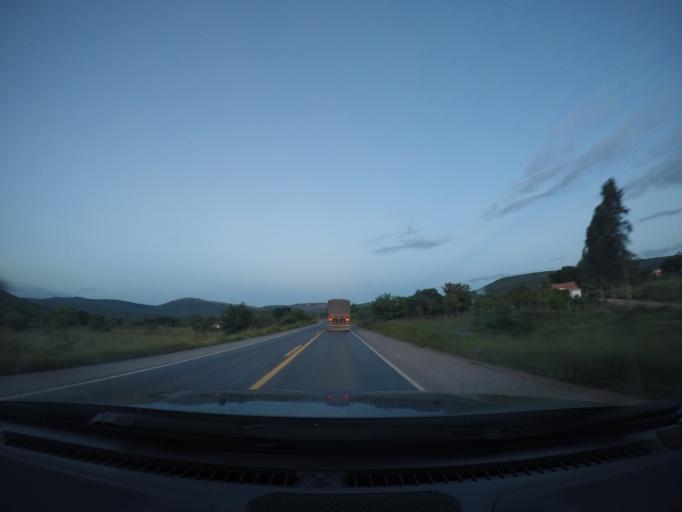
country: BR
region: Bahia
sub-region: Seabra
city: Seabra
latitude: -12.4855
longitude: -41.7241
